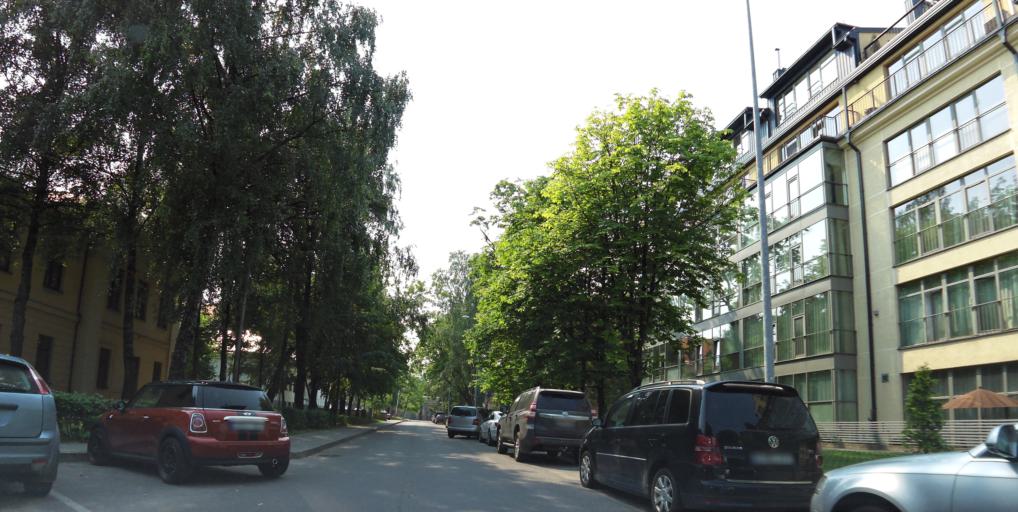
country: LT
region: Vilnius County
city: Rasos
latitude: 54.6998
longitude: 25.3138
